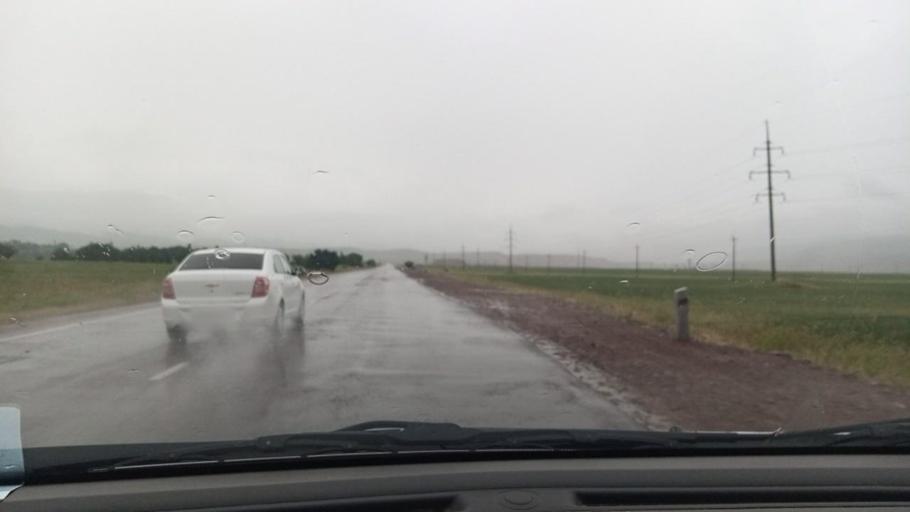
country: UZ
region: Toshkent
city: Angren
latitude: 41.0366
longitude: 70.1455
